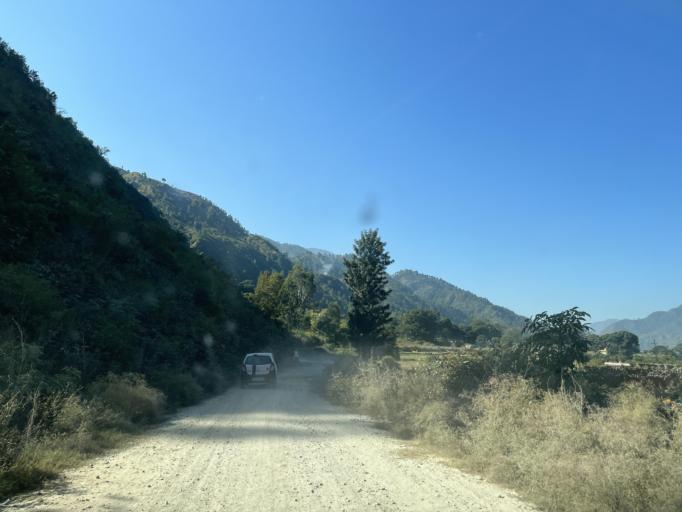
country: IN
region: Uttarakhand
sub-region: Almora
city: Ranikhet
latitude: 29.5524
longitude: 79.3916
